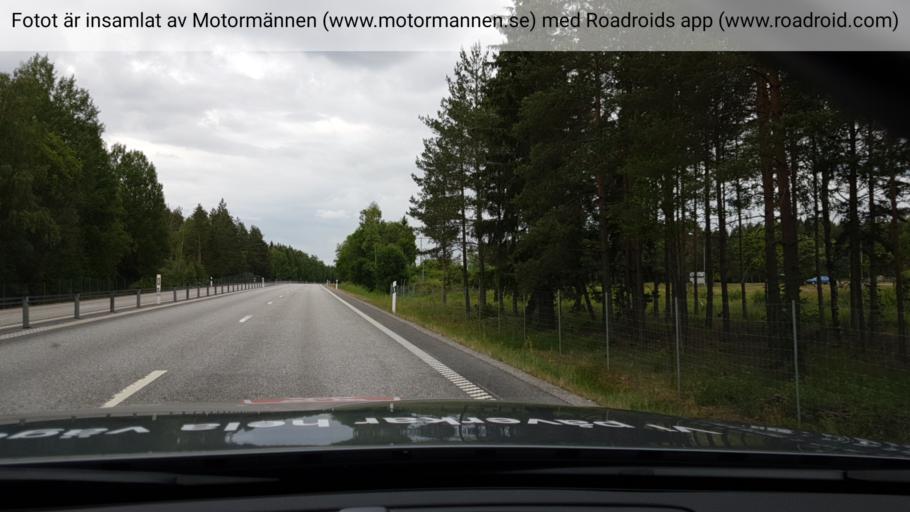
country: SE
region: Vaestmanland
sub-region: Surahammars Kommun
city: Surahammar
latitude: 59.7170
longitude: 16.2406
